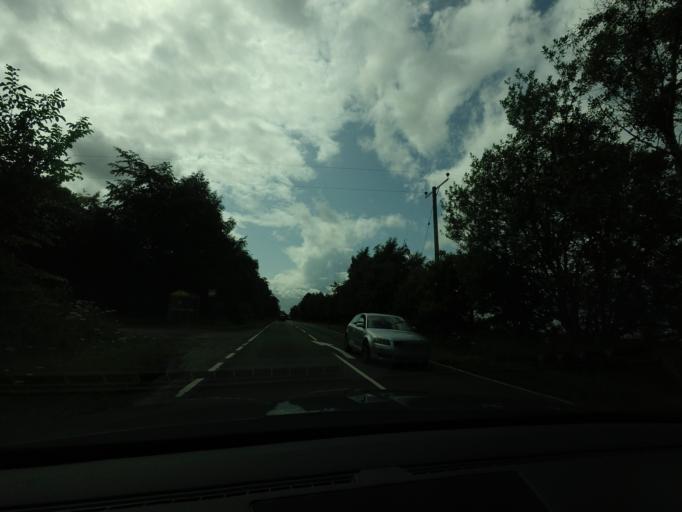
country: GB
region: Scotland
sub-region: Highland
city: Nairn
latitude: 57.5828
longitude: -3.7600
